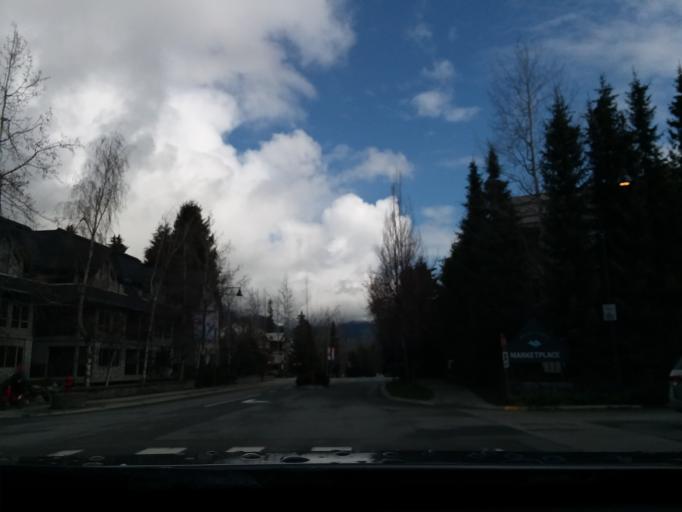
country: CA
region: British Columbia
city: Whistler
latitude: 50.1197
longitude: -122.9583
